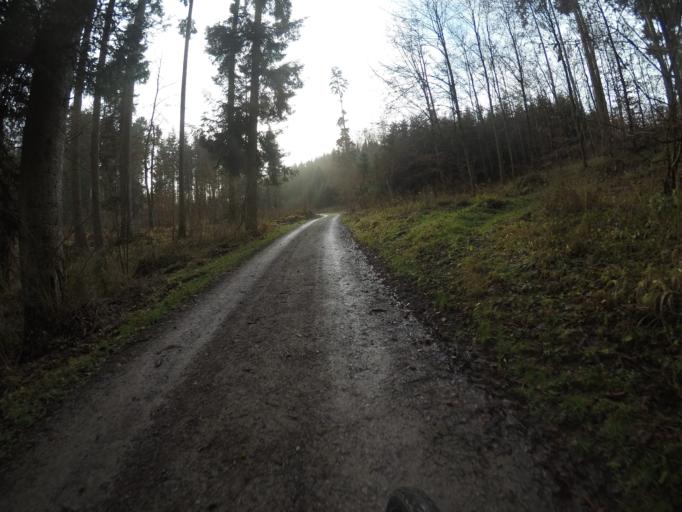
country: DE
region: Baden-Wuerttemberg
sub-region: Regierungsbezirk Stuttgart
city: Deckenpfronn
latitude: 48.6614
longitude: 8.8230
